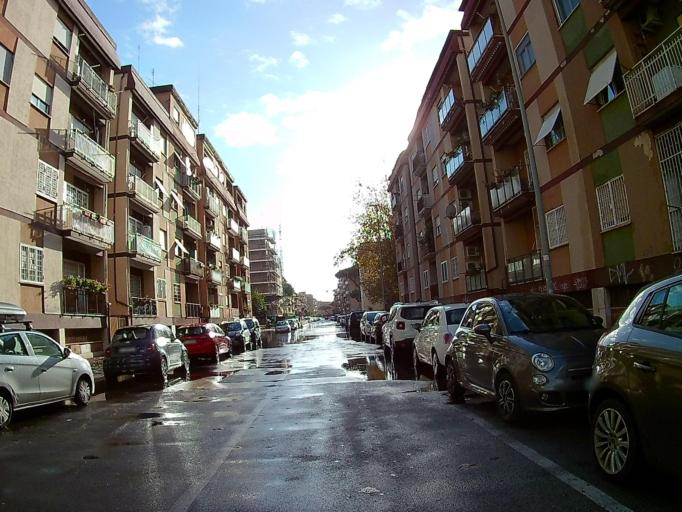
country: IT
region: Latium
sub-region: Citta metropolitana di Roma Capitale
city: Lido di Ostia
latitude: 41.7372
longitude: 12.2872
